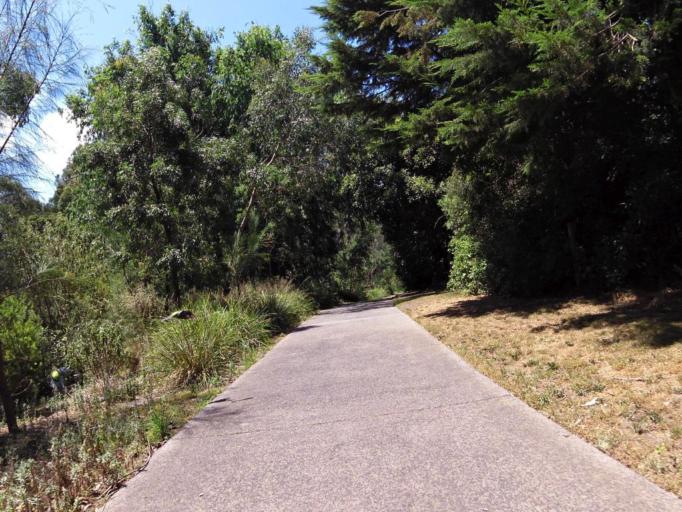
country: AU
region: Victoria
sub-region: Monash
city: Notting Hill
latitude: -37.8850
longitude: 145.1372
